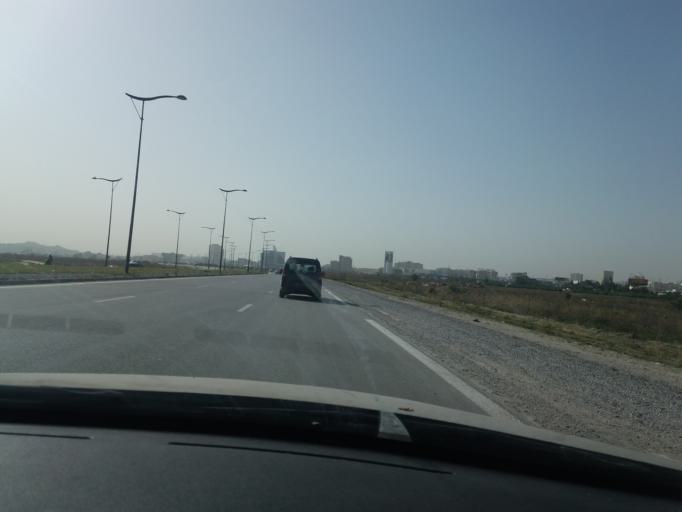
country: TN
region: Tunis
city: Tunis
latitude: 36.8189
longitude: 10.1977
